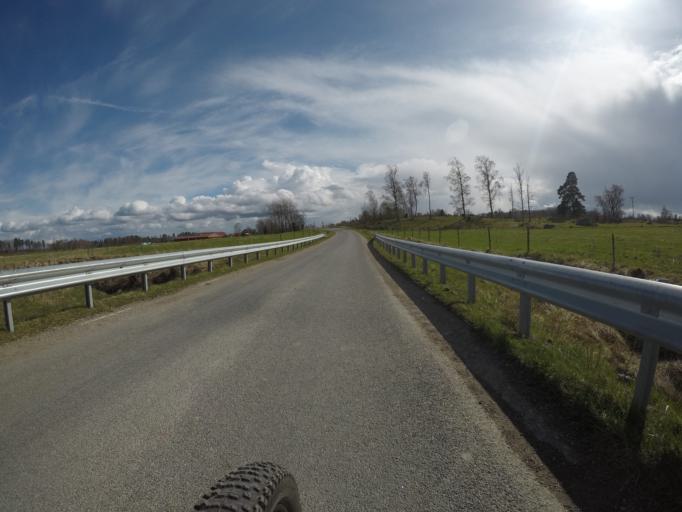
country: SE
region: Vaestmanland
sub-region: Kungsors Kommun
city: Kungsoer
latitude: 59.3001
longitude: 16.1387
